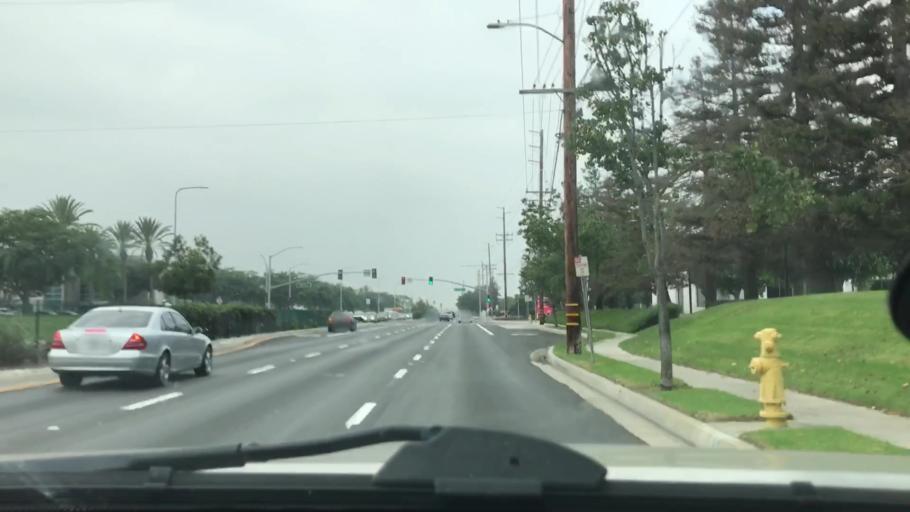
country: US
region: California
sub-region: Los Angeles County
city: Gardena
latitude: 33.8553
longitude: -118.3095
